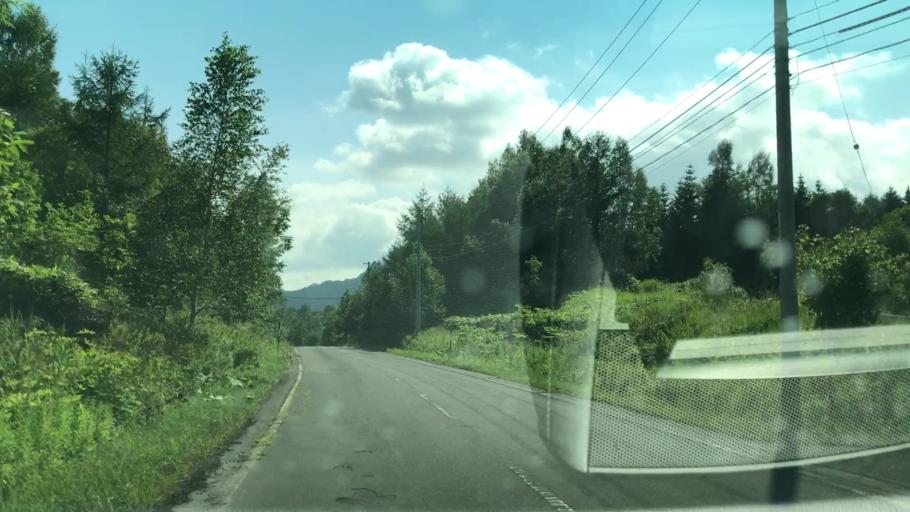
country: JP
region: Hokkaido
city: Shimo-furano
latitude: 42.8531
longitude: 142.4361
